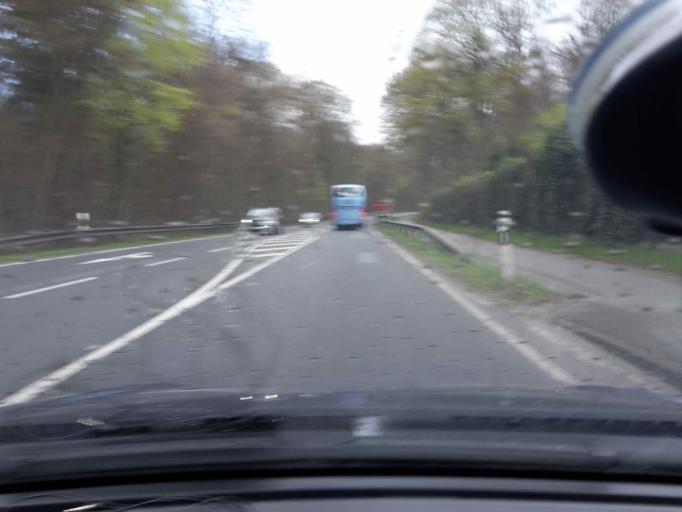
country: DE
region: Lower Saxony
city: Buxtehude
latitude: 53.4738
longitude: 9.6527
